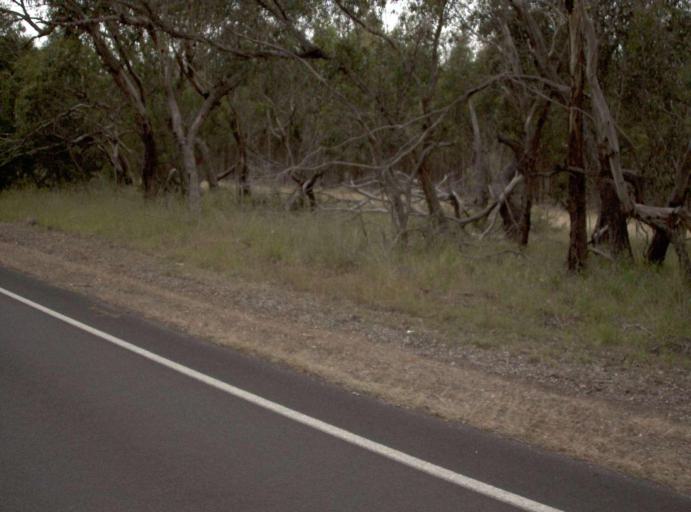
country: AU
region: Victoria
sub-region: Wellington
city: Sale
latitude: -38.4209
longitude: 146.9578
